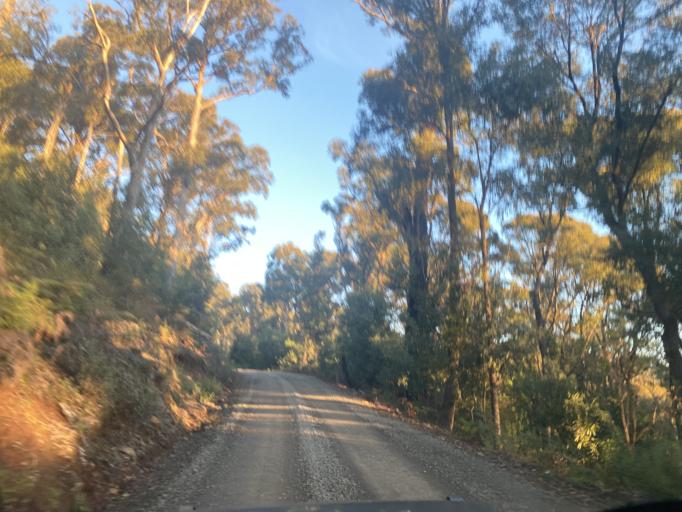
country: AU
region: Victoria
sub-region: Yarra Ranges
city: Healesville
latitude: -37.4254
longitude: 145.5283
